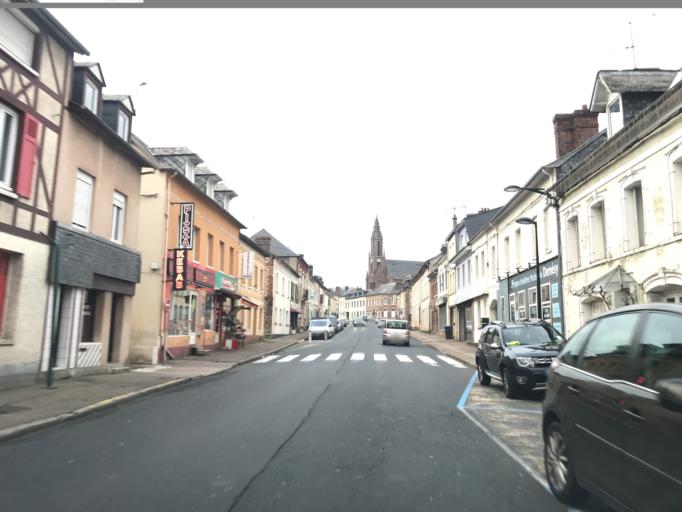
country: FR
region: Haute-Normandie
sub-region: Departement de l'Eure
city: Fleury-sur-Andelle
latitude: 49.3614
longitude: 1.3564
